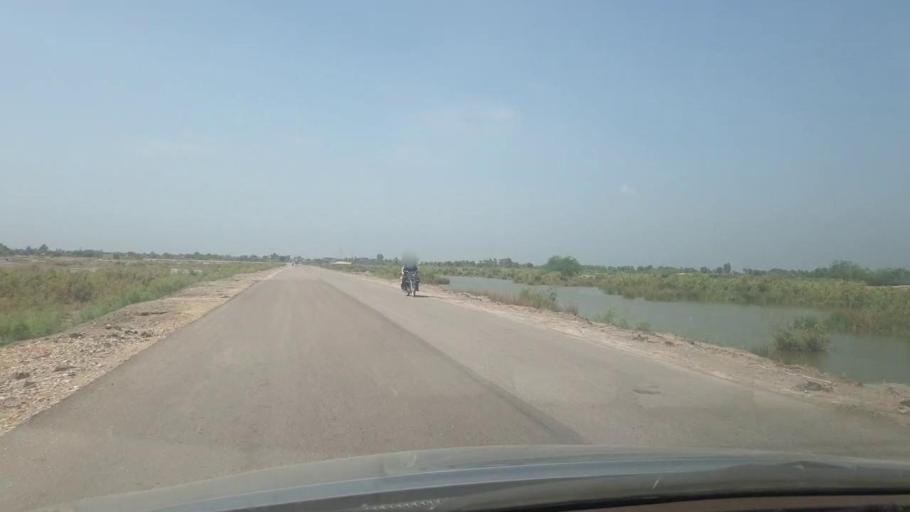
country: PK
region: Sindh
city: Bozdar
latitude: 27.2350
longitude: 68.5706
